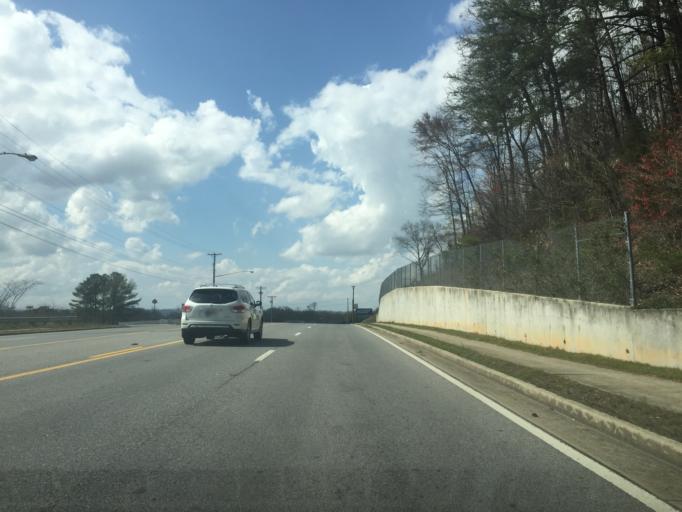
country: US
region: Georgia
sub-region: Catoosa County
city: Indian Springs
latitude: 34.9868
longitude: -85.1889
